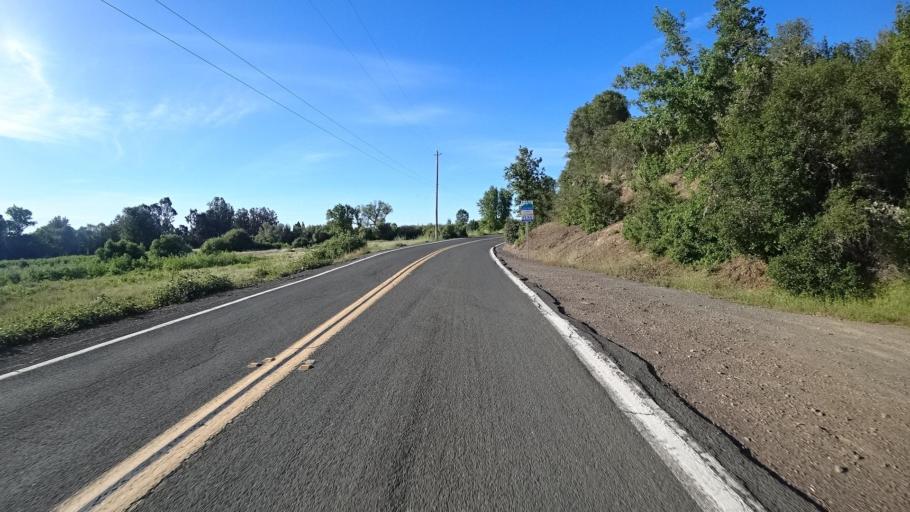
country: US
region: California
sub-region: Lake County
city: North Lakeport
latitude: 39.0901
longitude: -122.9496
